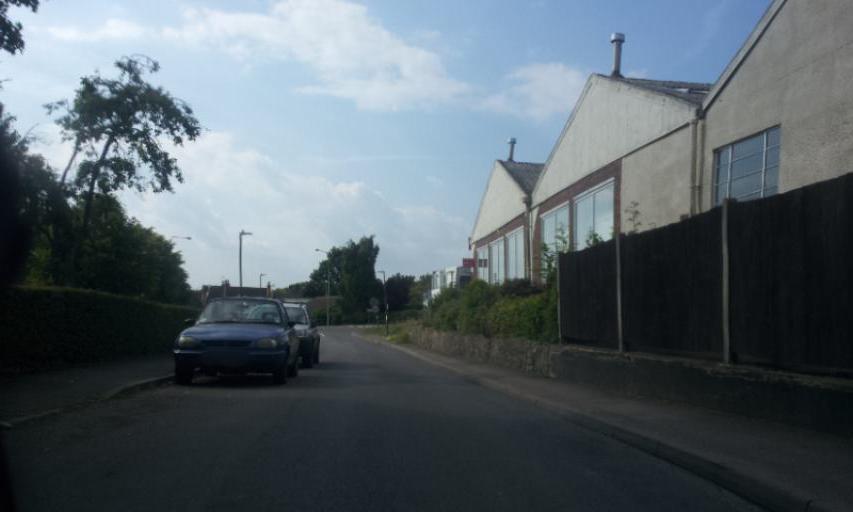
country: GB
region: England
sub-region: Kent
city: Harrietsham
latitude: 51.2413
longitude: 0.6770
